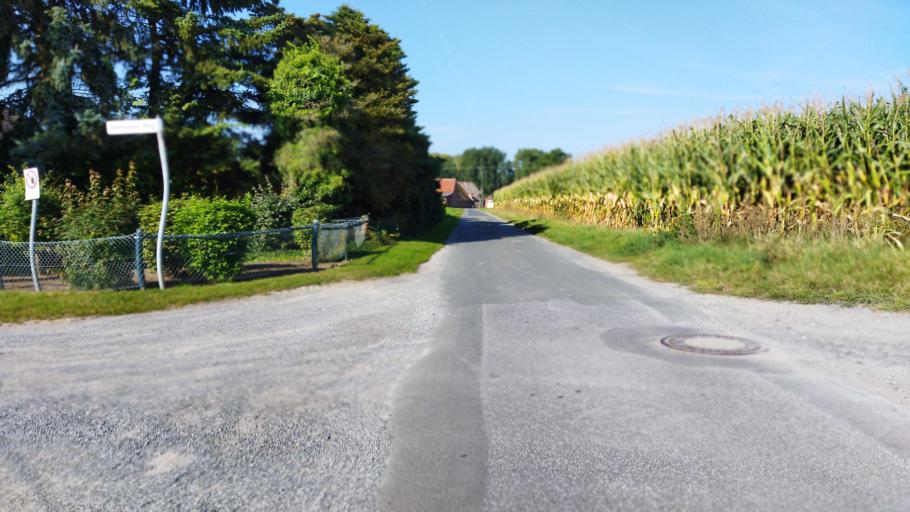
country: DE
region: North Rhine-Westphalia
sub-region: Regierungsbezirk Munster
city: Lienen
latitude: 52.1483
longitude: 7.9473
